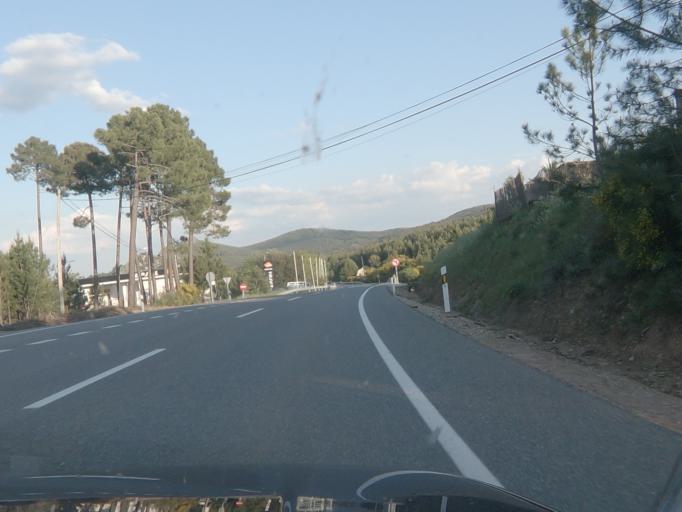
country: PT
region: Portalegre
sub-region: Portalegre
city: Sao Juliao
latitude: 39.3471
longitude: -7.2996
